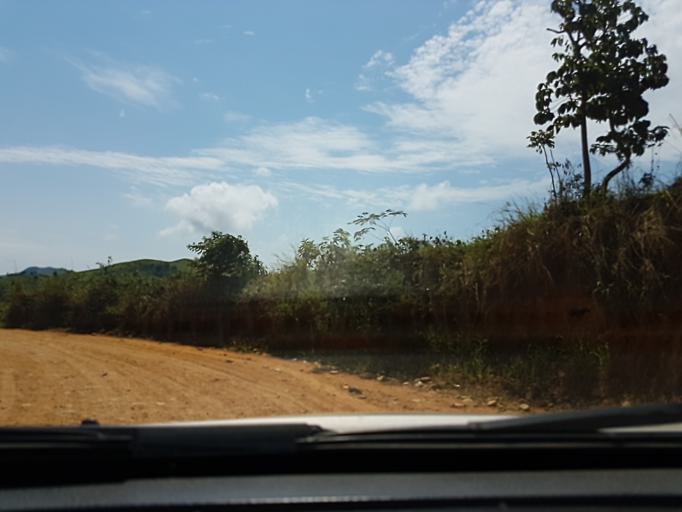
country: RW
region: Western Province
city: Cyangugu
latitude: -2.7034
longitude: 28.9209
